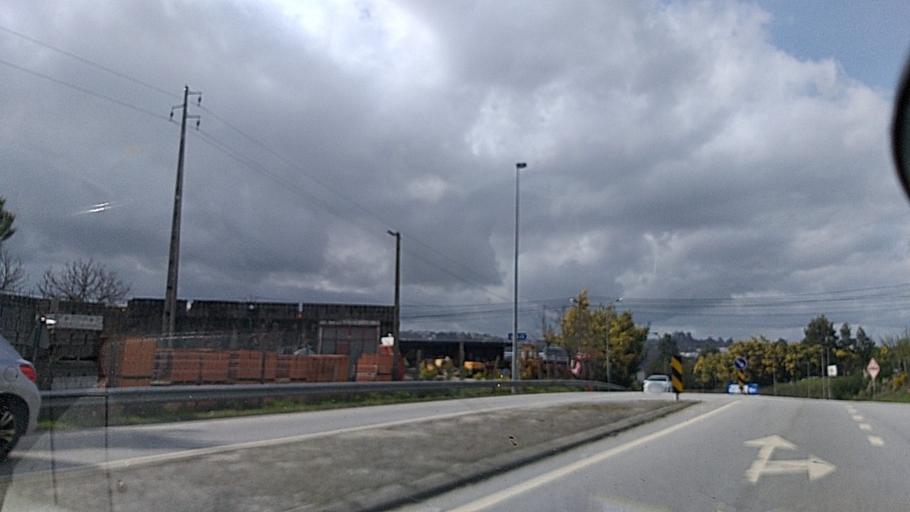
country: PT
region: Viseu
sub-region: Mangualde
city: Mangualde
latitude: 40.6200
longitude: -7.7587
